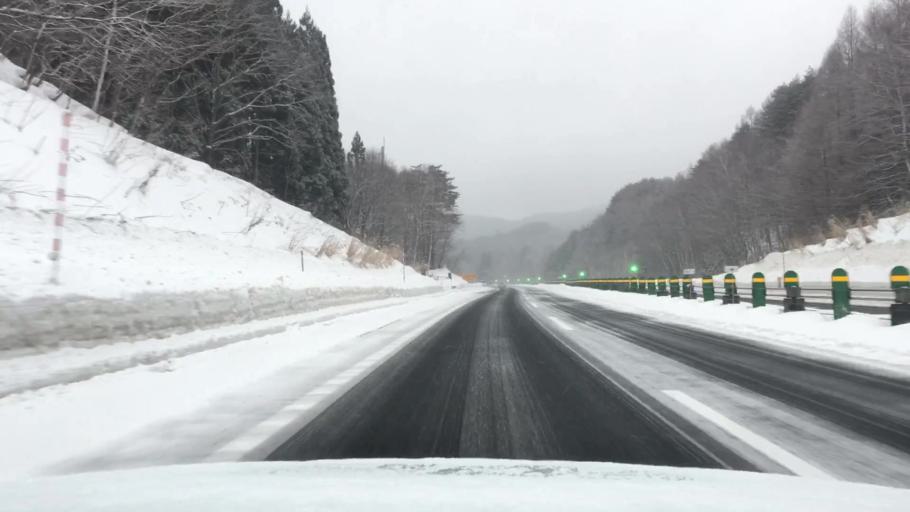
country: JP
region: Akita
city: Hanawa
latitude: 40.1186
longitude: 141.0150
